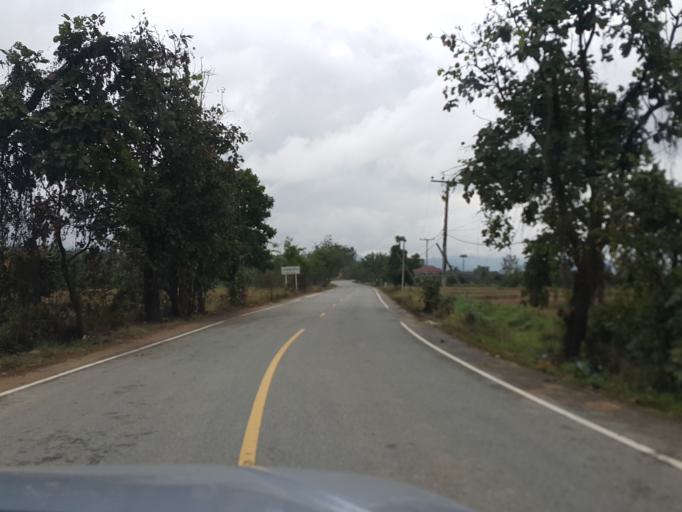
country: TH
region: Lamphun
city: Ban Thi
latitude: 18.6796
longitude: 99.1401
